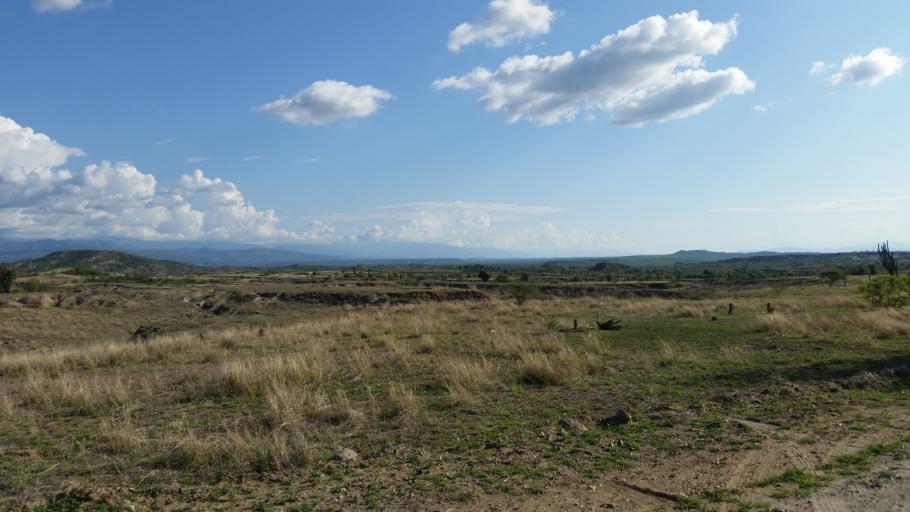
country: CO
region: Huila
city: Baraya
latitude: 3.2363
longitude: -75.1117
